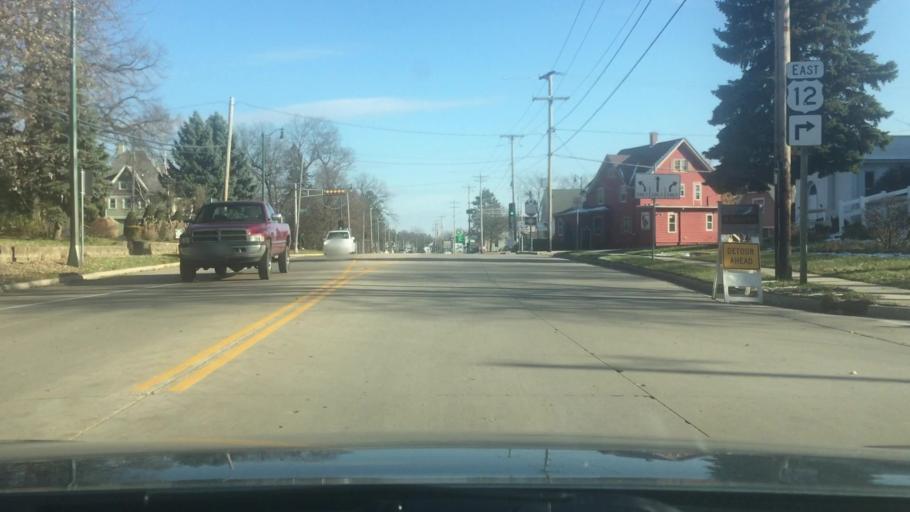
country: US
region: Wisconsin
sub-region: Jefferson County
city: Fort Atkinson
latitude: 42.9332
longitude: -88.8445
